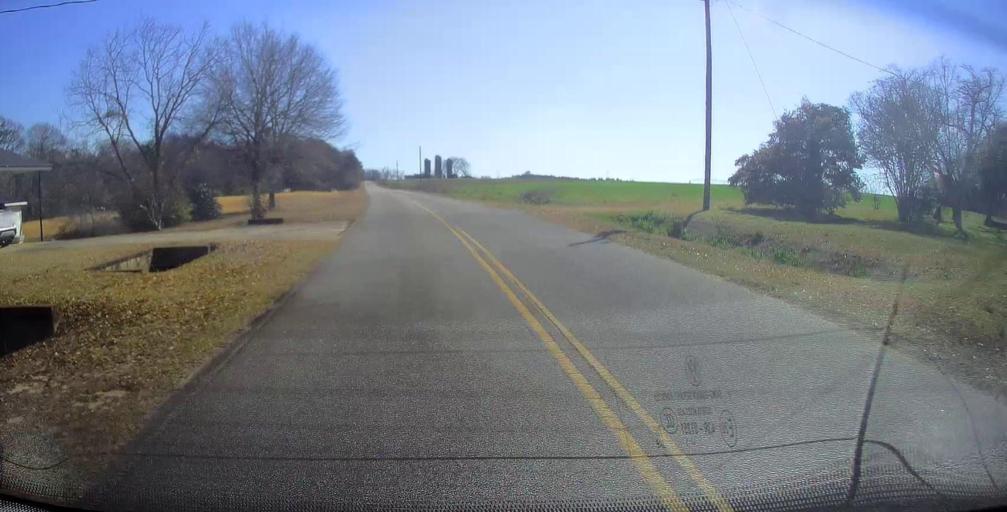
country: US
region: Georgia
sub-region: Peach County
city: Fort Valley
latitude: 32.6177
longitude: -83.8349
